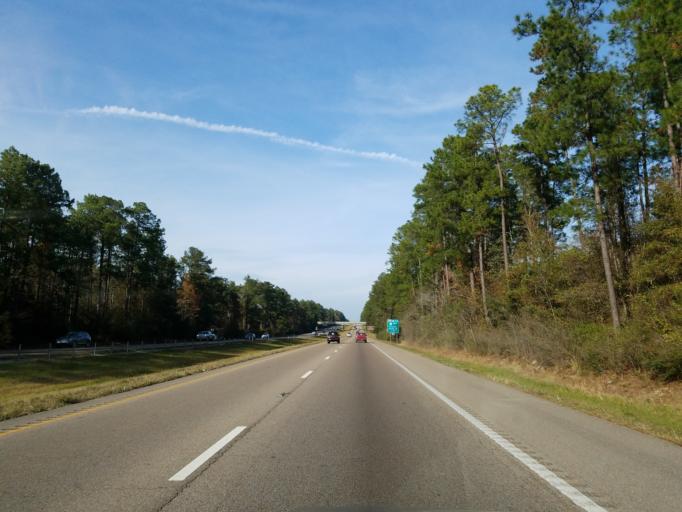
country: US
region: Mississippi
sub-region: Lamar County
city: West Hattiesburg
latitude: 31.2995
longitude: -89.3525
